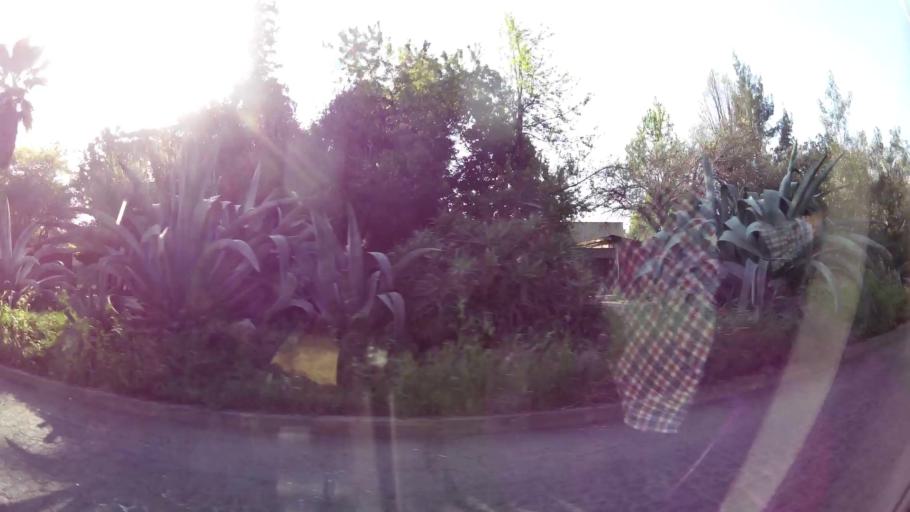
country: CL
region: Santiago Metropolitan
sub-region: Provincia de Santiago
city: Santiago
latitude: -33.4179
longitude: -70.6477
